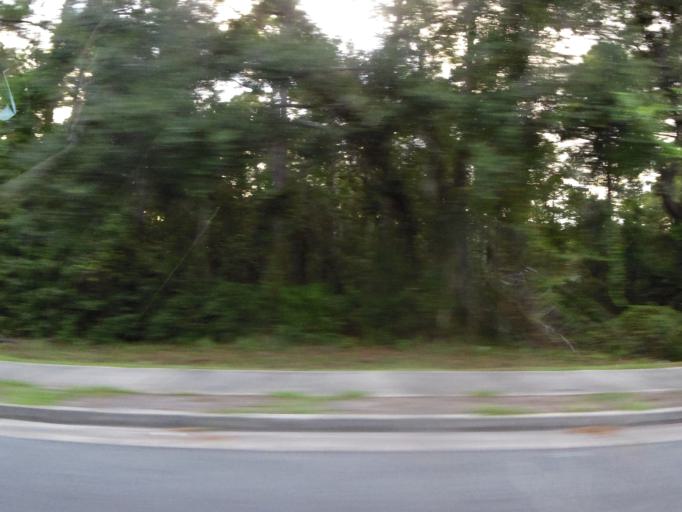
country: US
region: Georgia
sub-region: Glynn County
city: Country Club Estates
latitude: 31.2179
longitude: -81.4796
